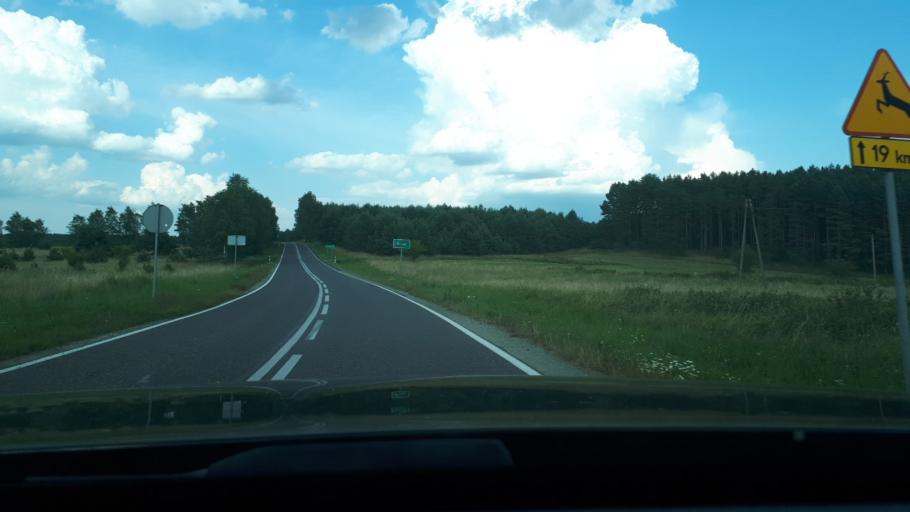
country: PL
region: Warmian-Masurian Voivodeship
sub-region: Powiat olsztynski
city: Stawiguda
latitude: 53.5368
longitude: 20.4815
